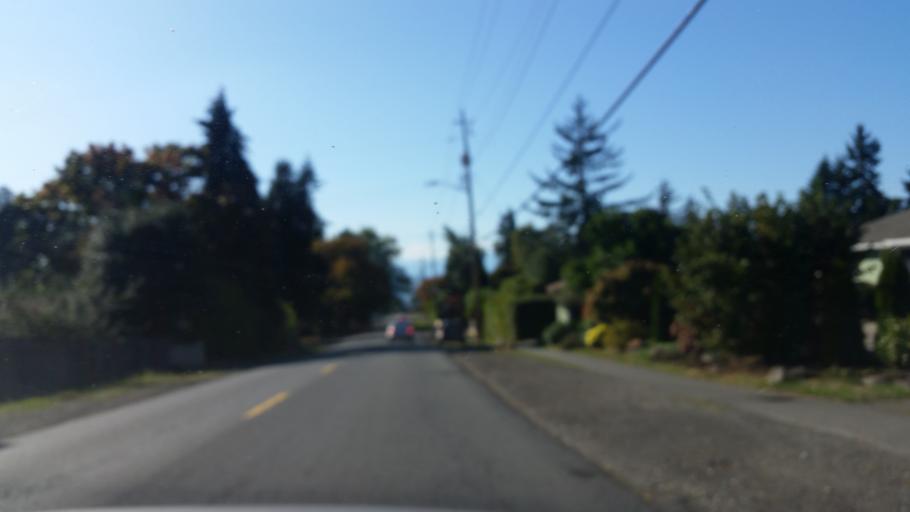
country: US
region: Washington
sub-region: King County
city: Shoreline
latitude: 47.7196
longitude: -122.3585
